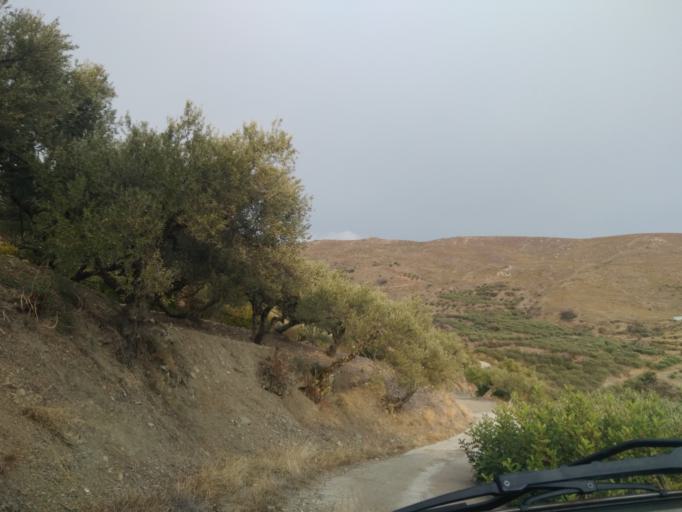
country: GR
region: Crete
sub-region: Nomos Lasithiou
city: Makry-Gialos
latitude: 35.1227
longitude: 26.0233
